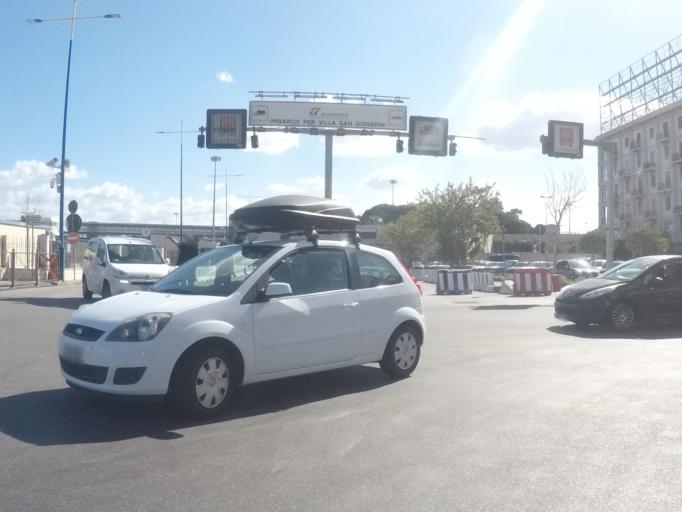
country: IT
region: Sicily
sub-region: Messina
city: Messina
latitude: 38.1878
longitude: 15.5611
